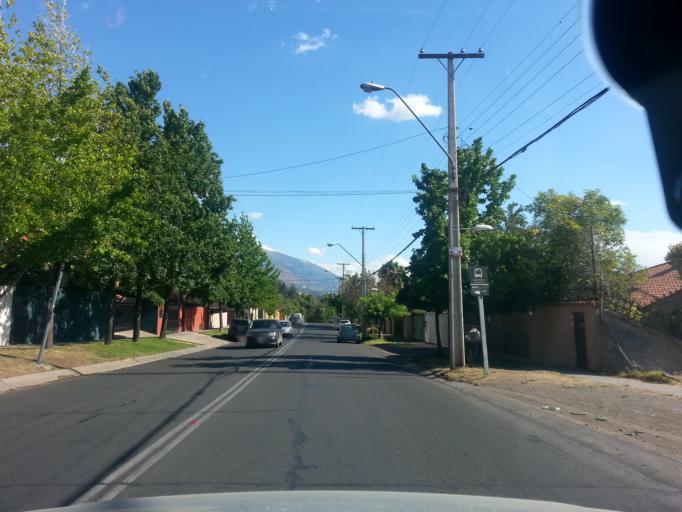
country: CL
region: Santiago Metropolitan
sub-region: Provincia de Santiago
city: Villa Presidente Frei, Nunoa, Santiago, Chile
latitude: -33.4137
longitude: -70.5299
